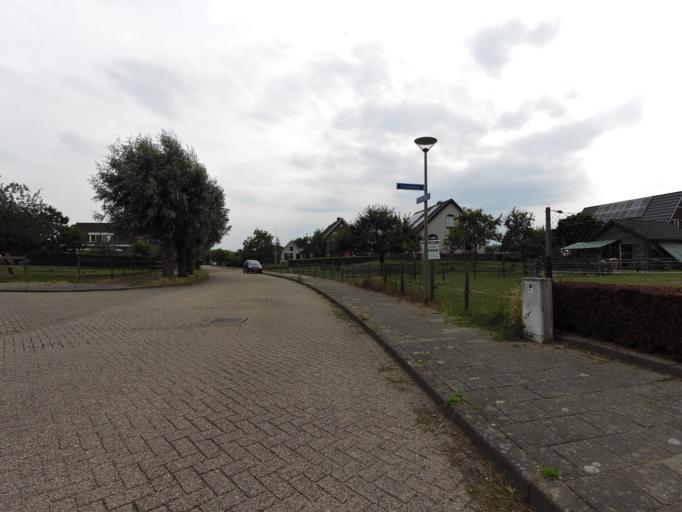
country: NL
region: Gelderland
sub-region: Gemeente Zevenaar
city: Zevenaar
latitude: 51.8650
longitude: 6.0403
